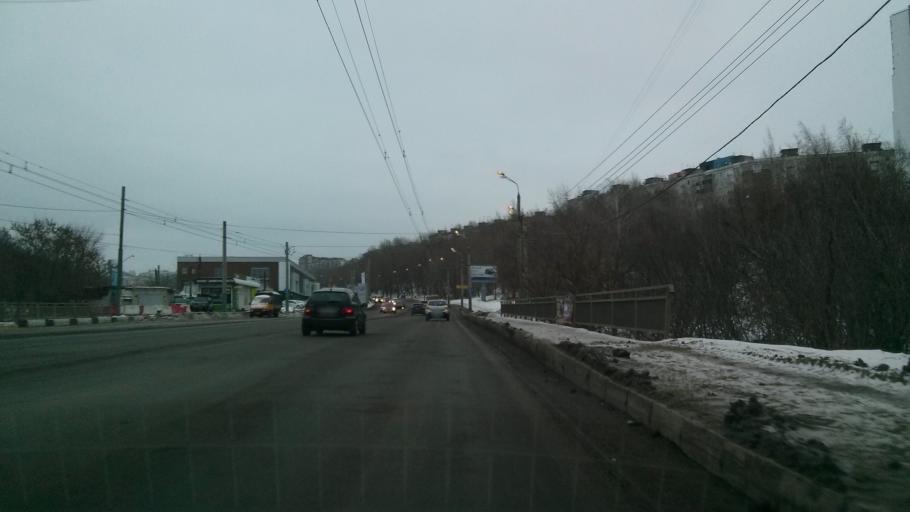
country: RU
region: Nizjnij Novgorod
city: Afonino
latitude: 56.3013
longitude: 44.0549
